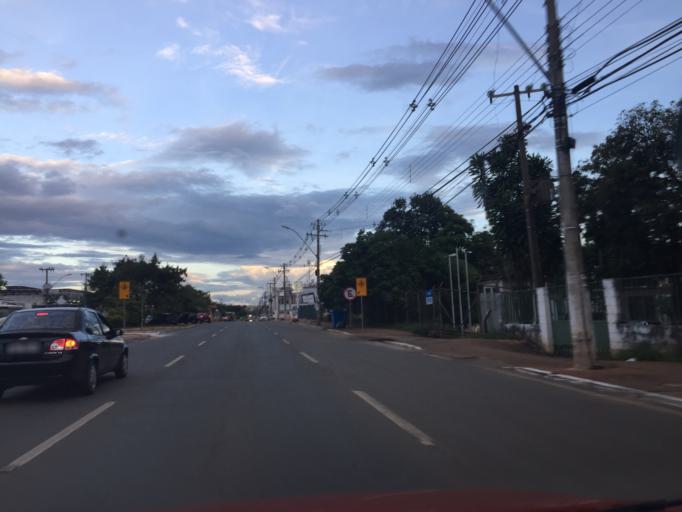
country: BR
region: Federal District
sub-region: Brasilia
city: Brasilia
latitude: -15.8067
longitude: -47.9563
